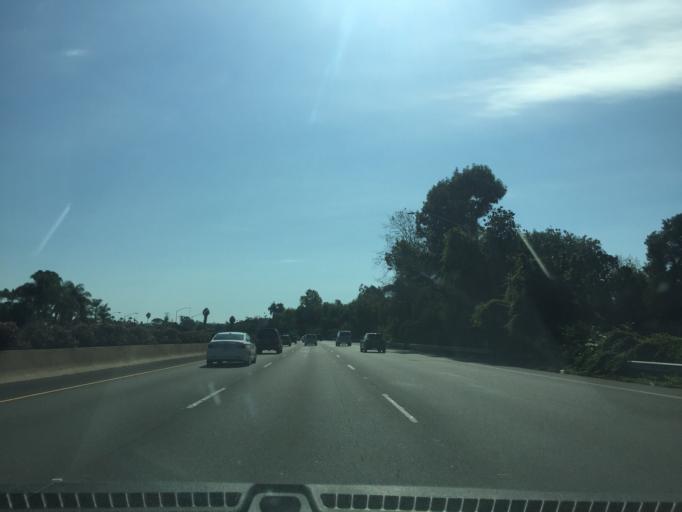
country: US
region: California
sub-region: Santa Barbara County
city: Mission Canyon
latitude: 34.4343
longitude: -119.7489
